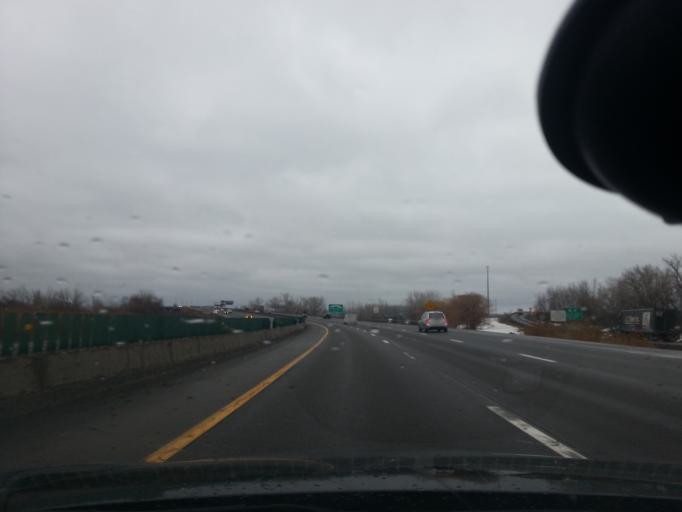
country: US
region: New York
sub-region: Onondaga County
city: Galeville
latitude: 43.0814
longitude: -76.1729
